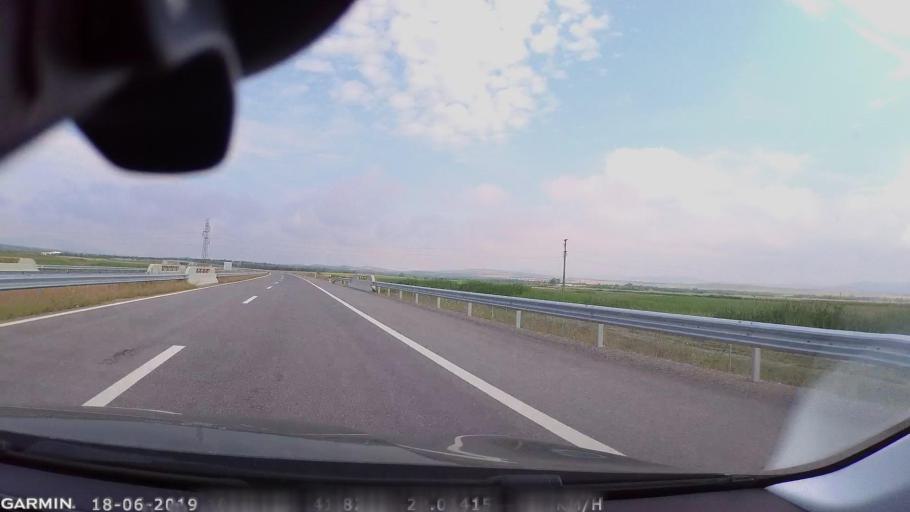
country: MK
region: Sveti Nikole
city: Sveti Nikole
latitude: 41.8203
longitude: 22.0142
